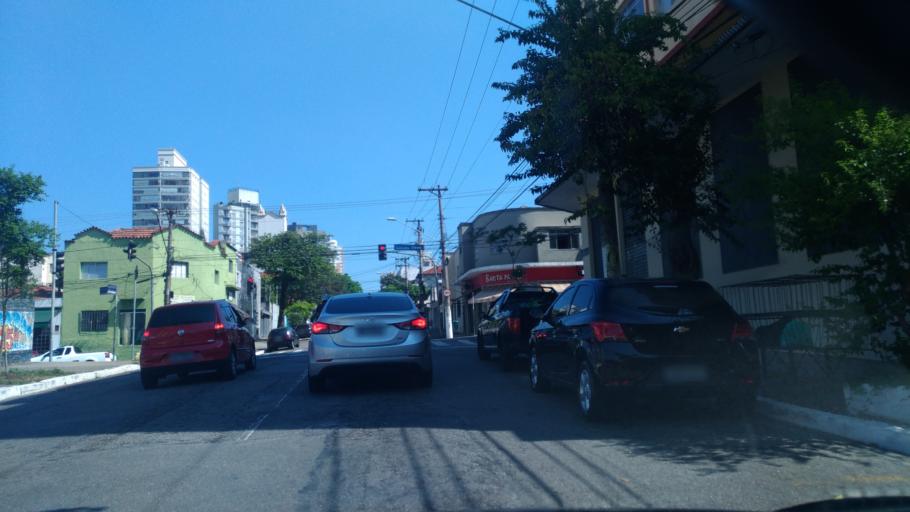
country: BR
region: Sao Paulo
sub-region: Sao Paulo
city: Sao Paulo
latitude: -23.5891
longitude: -46.6040
